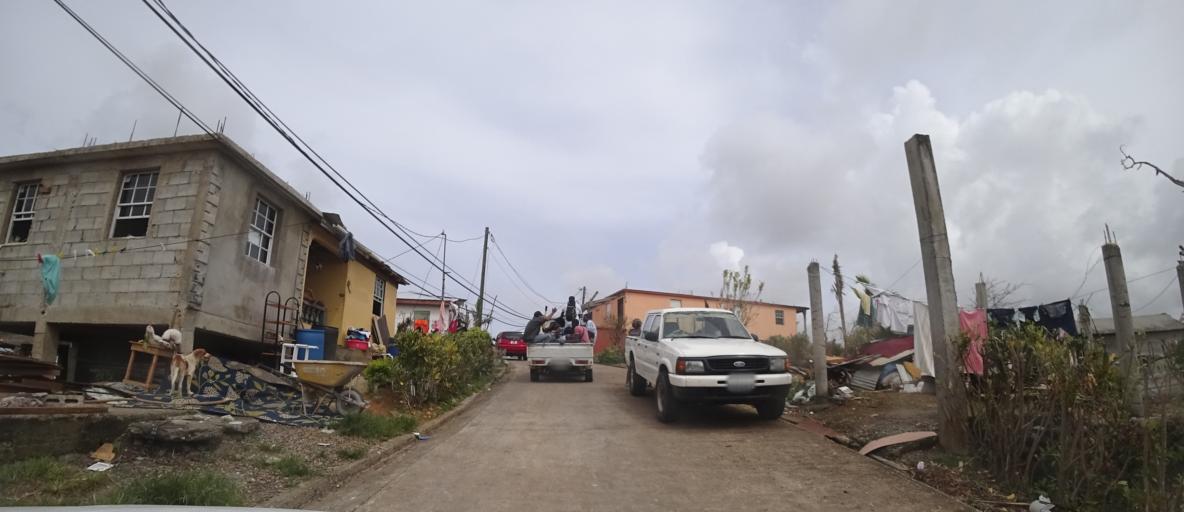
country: DM
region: Saint Andrew
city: Calibishie
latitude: 15.5852
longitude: -61.3727
